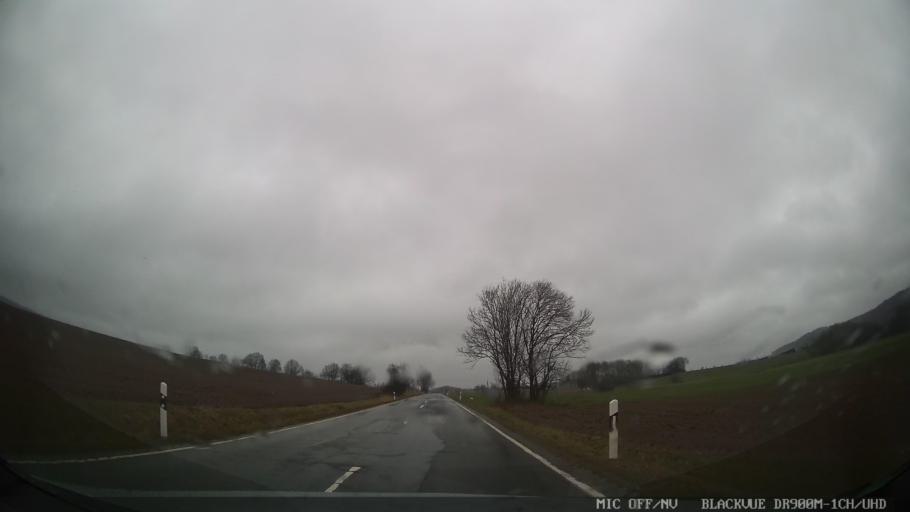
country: DE
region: Rheinland-Pfalz
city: Meckenbach
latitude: 49.6296
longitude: 7.1030
